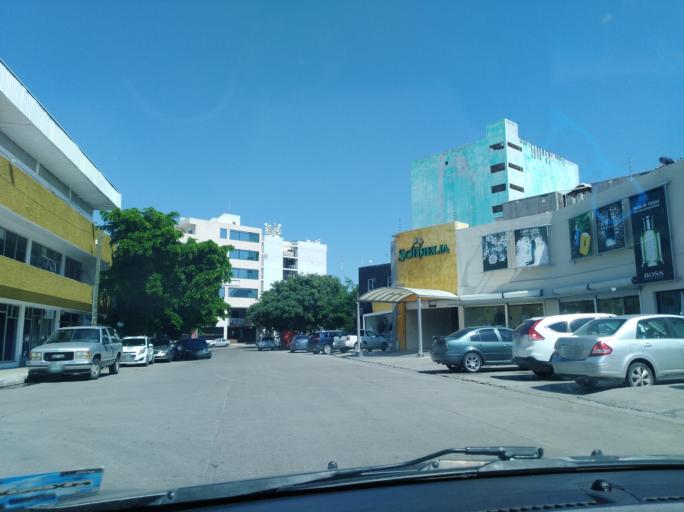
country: MX
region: Sinaloa
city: Culiacan
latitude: 24.7944
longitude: -107.4137
